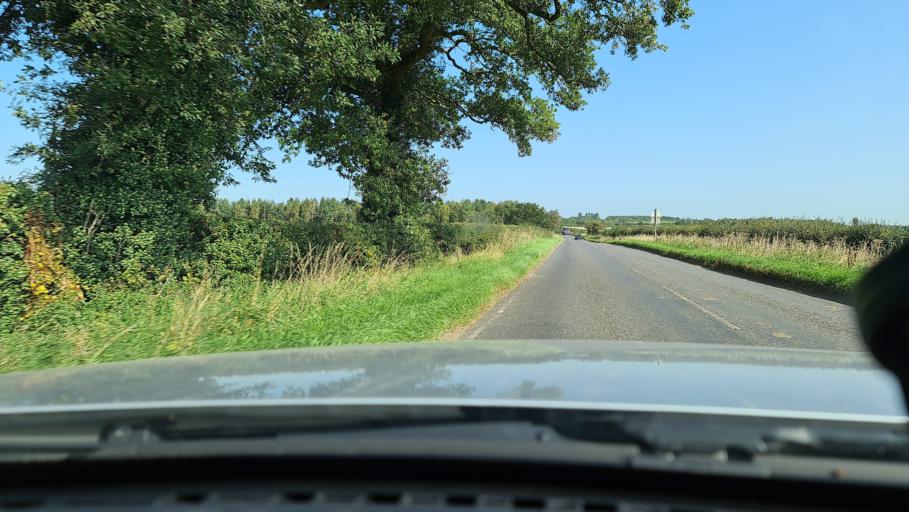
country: GB
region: England
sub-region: Northamptonshire
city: Brackley
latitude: 52.1029
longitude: -1.2017
